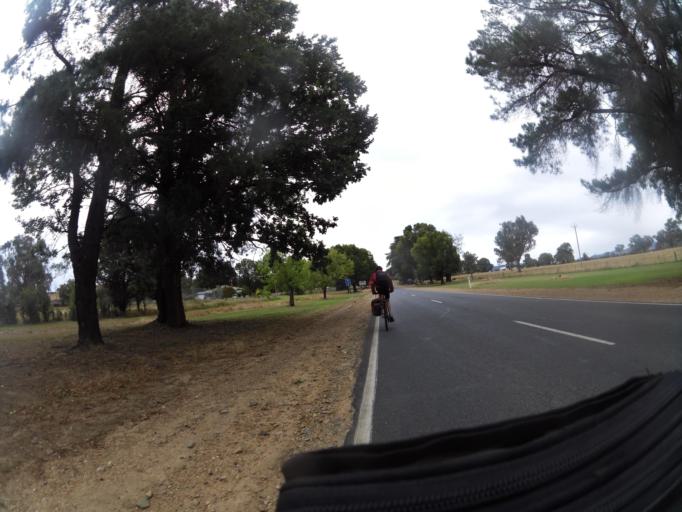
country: AU
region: New South Wales
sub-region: Snowy River
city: Jindabyne
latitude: -36.1850
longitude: 147.9199
